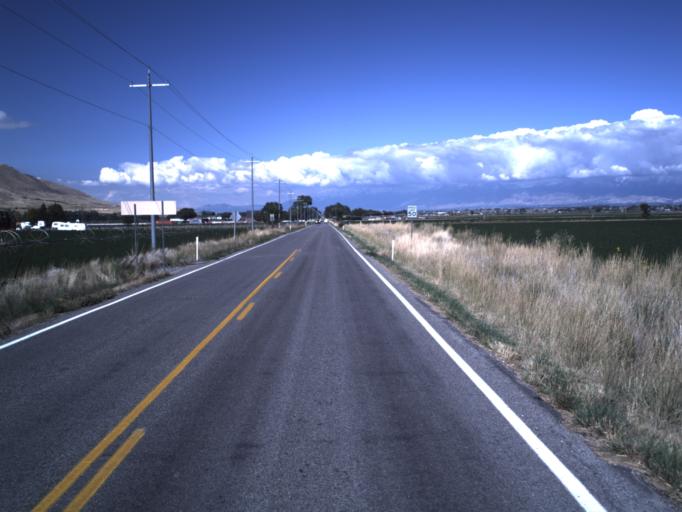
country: US
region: Utah
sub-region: Utah County
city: West Mountain
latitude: 40.0418
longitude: -111.7872
